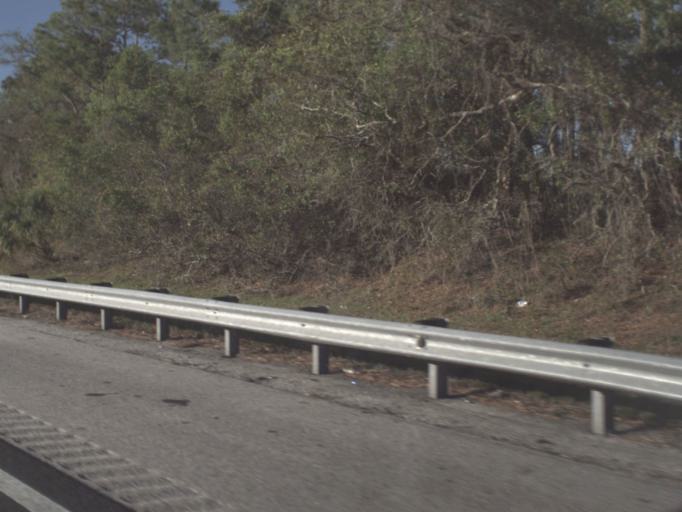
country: US
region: Florida
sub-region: Flagler County
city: Palm Coast
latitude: 29.6506
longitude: -81.2756
